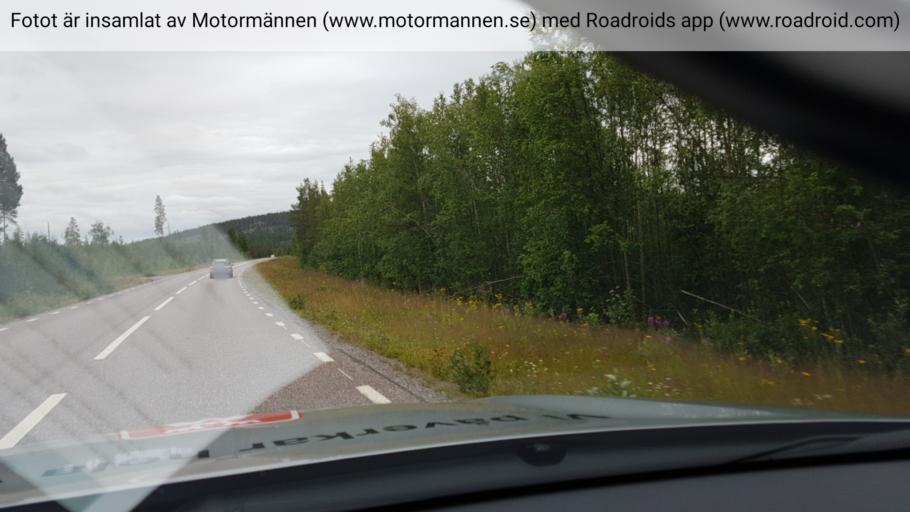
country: SE
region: Norrbotten
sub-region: Gallivare Kommun
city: Gaellivare
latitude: 67.0334
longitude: 21.7066
